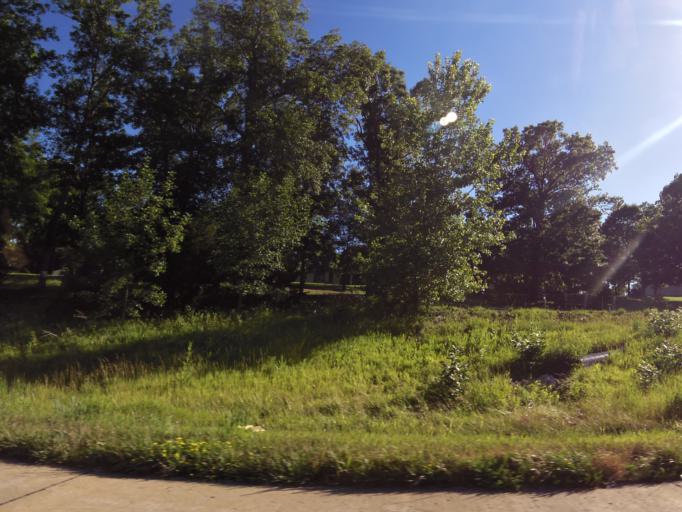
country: US
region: Missouri
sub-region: Ralls County
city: New London
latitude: 39.5227
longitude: -91.3461
